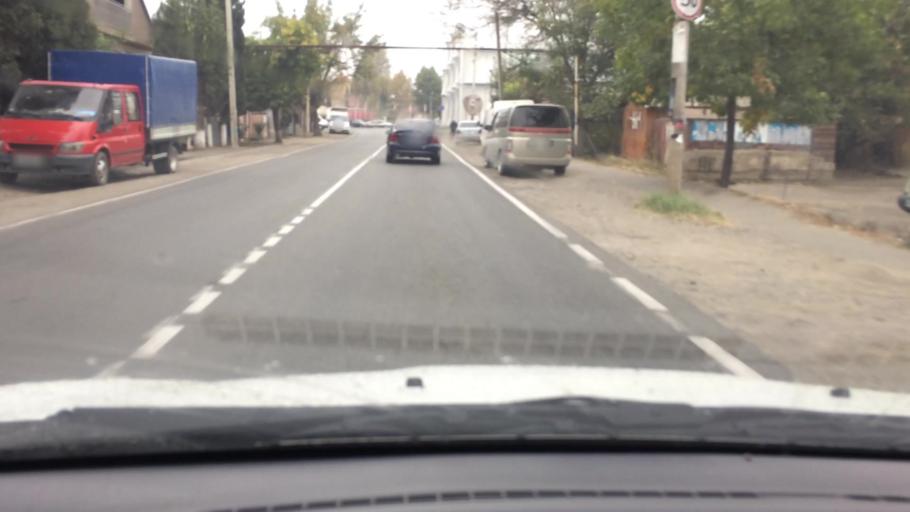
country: GE
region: Kvemo Kartli
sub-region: Marneuli
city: Marneuli
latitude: 41.4861
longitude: 44.7997
